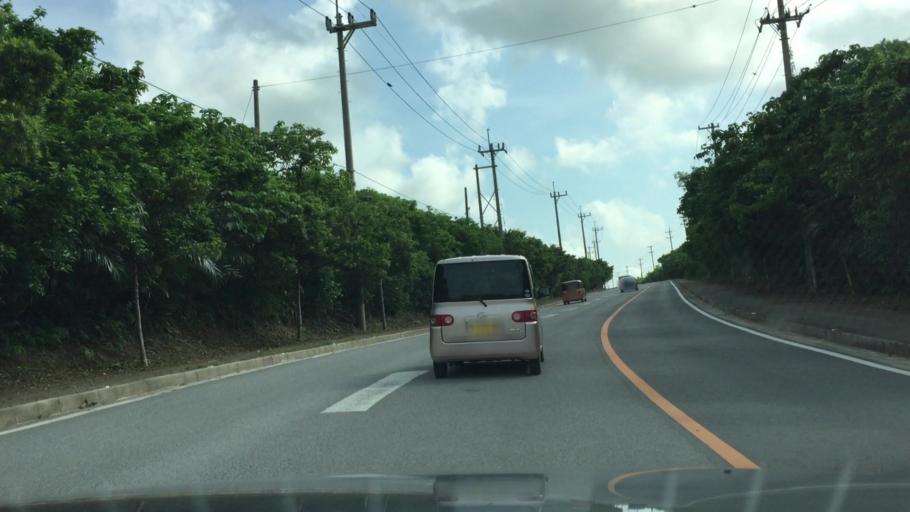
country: JP
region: Okinawa
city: Ishigaki
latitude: 24.4297
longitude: 124.2476
